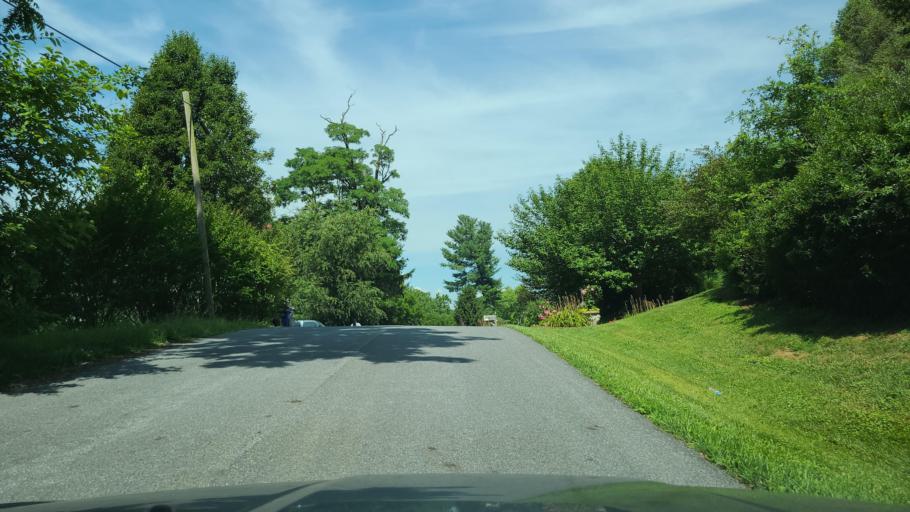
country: US
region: Maryland
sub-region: Frederick County
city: Green Valley
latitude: 39.3090
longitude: -77.2956
